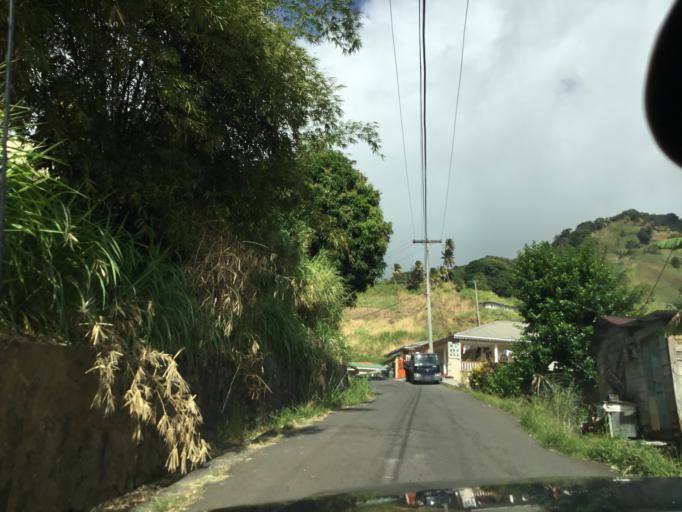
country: VC
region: Saint George
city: Kingstown
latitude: 13.1707
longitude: -61.2196
